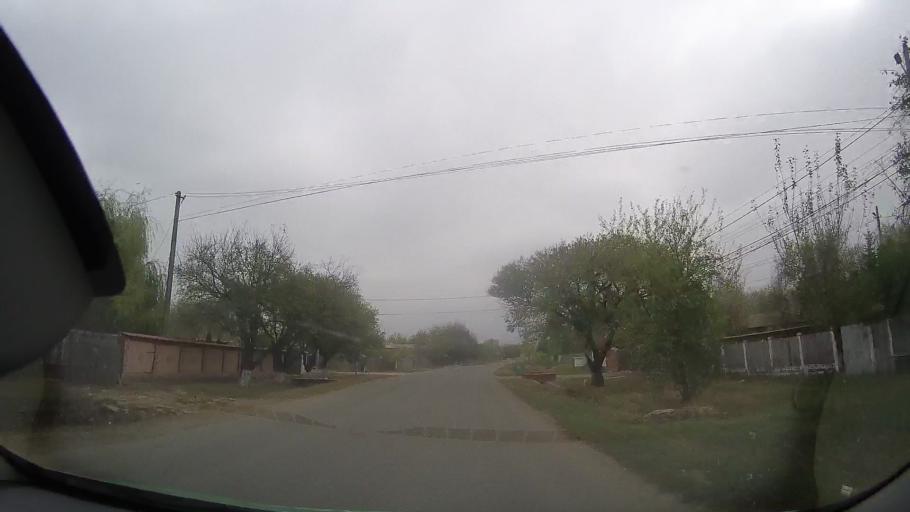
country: RO
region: Buzau
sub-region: Comuna Glodeanu-Silistea
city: Glodeanu-Silistea
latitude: 44.8209
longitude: 26.8340
